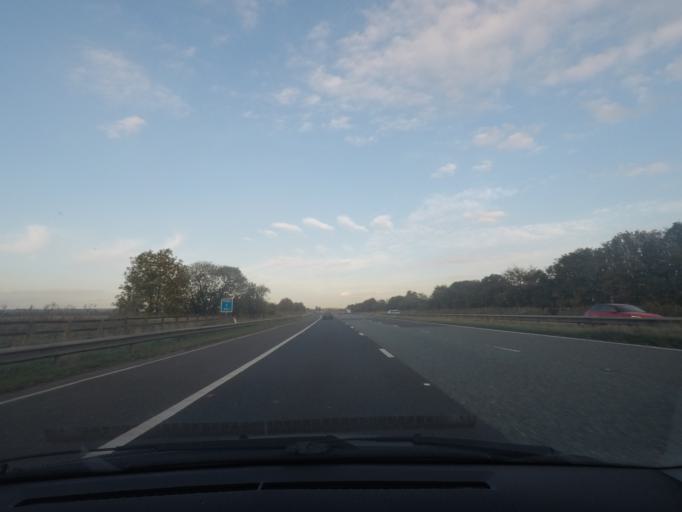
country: GB
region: England
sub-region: North Lincolnshire
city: Brigg
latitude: 53.5627
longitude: -0.4892
